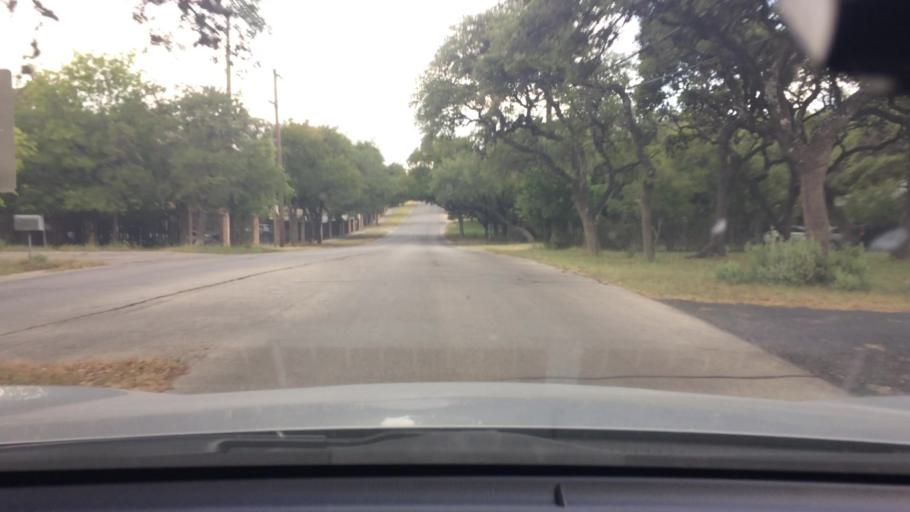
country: US
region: Texas
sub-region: Bexar County
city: Hollywood Park
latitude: 29.5568
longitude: -98.4689
